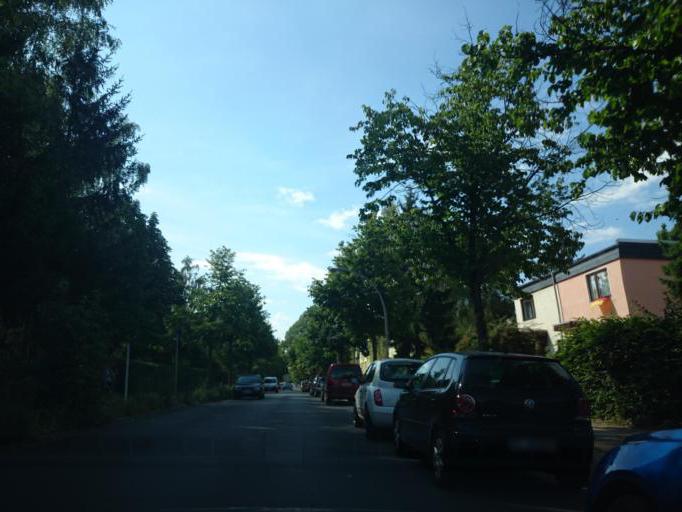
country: DE
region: Berlin
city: Lichtenrade
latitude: 52.3978
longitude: 13.3894
